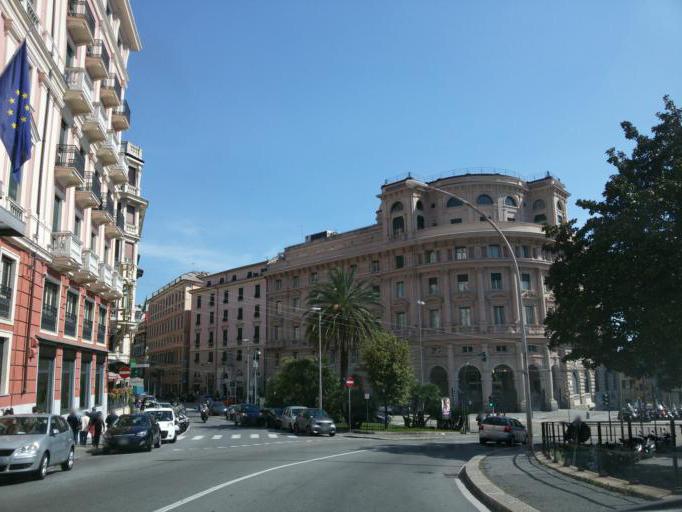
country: IT
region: Liguria
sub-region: Provincia di Genova
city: Genoa
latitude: 44.4171
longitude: 8.9228
